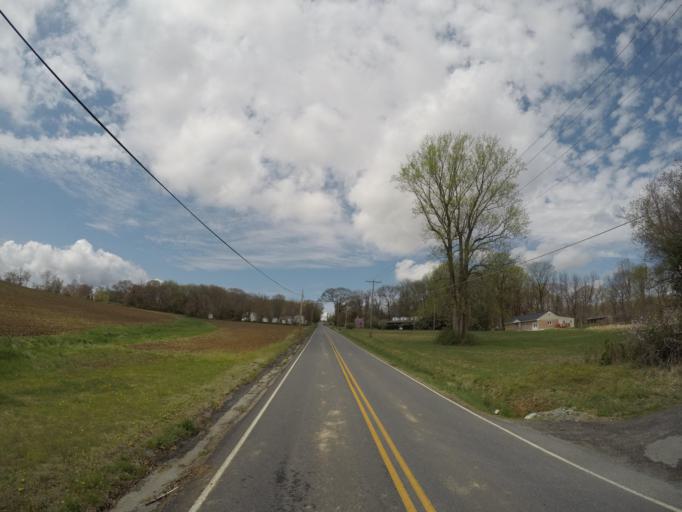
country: US
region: Maryland
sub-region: Cecil County
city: Perryville
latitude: 39.5867
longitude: -76.0584
